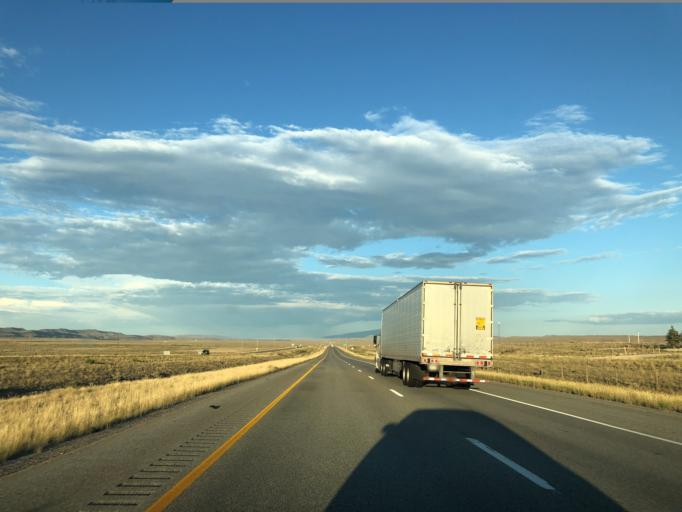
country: US
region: Wyoming
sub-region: Carbon County
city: Rawlins
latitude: 41.7726
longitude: -107.0672
